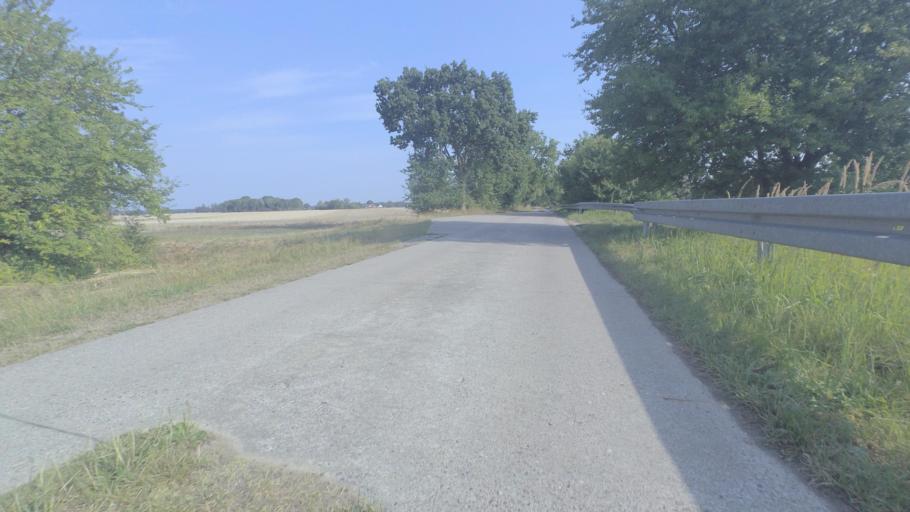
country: DE
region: Mecklenburg-Vorpommern
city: Wittenhagen
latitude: 54.1744
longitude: 13.0738
